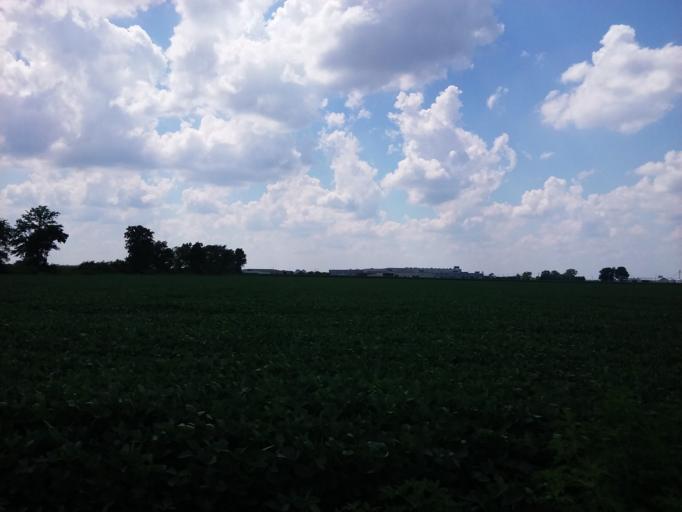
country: US
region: Ohio
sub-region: Wood County
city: Bowling Green
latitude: 41.3821
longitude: -83.5909
